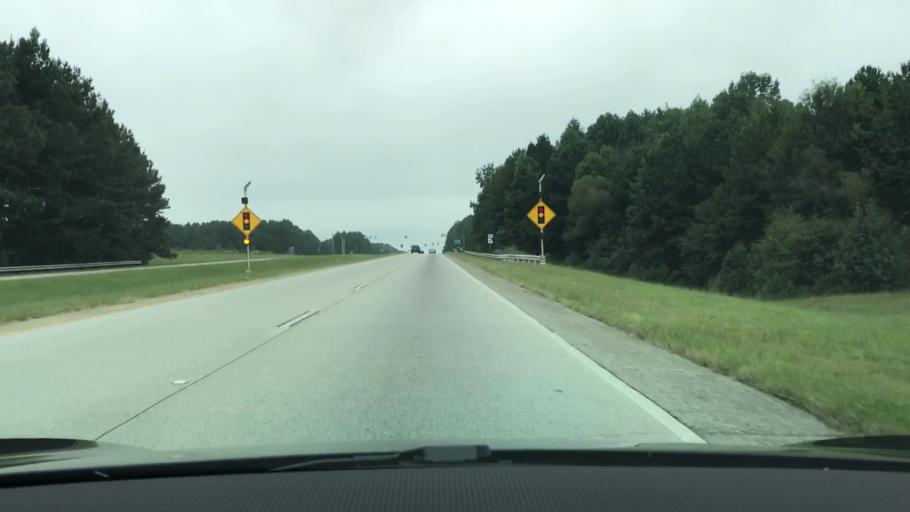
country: US
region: Georgia
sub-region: Barrow County
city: Statham
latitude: 33.9553
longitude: -83.6029
